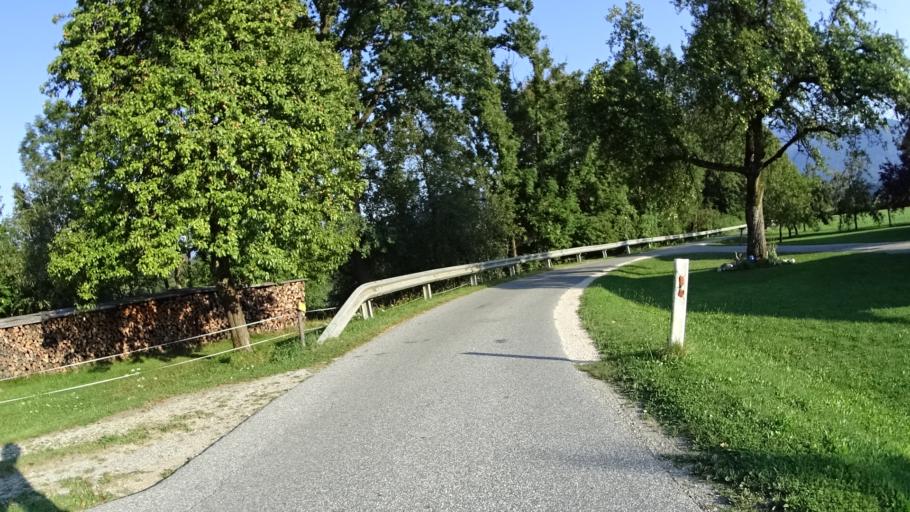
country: AT
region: Carinthia
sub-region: Politischer Bezirk Villach Land
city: Sankt Jakob
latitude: 46.5644
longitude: 14.0582
